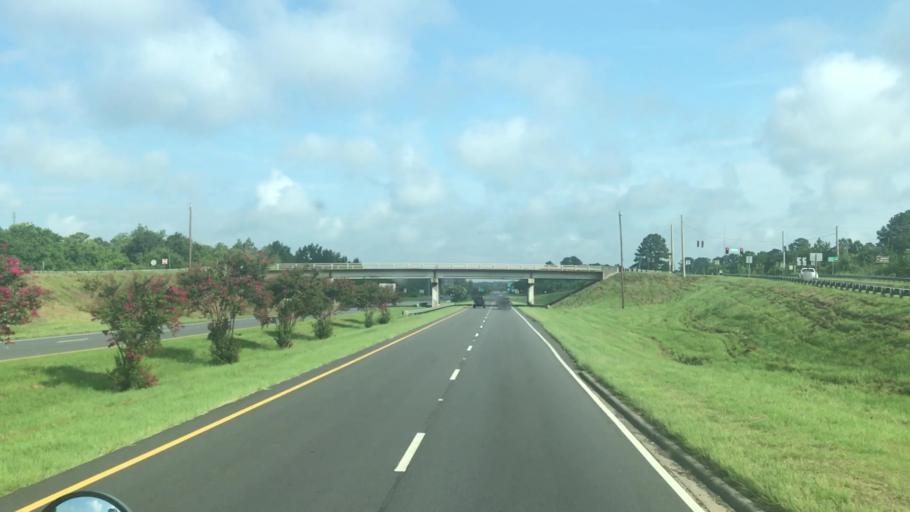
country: US
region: Georgia
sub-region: Decatur County
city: Bainbridge
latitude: 30.9105
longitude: -84.5930
